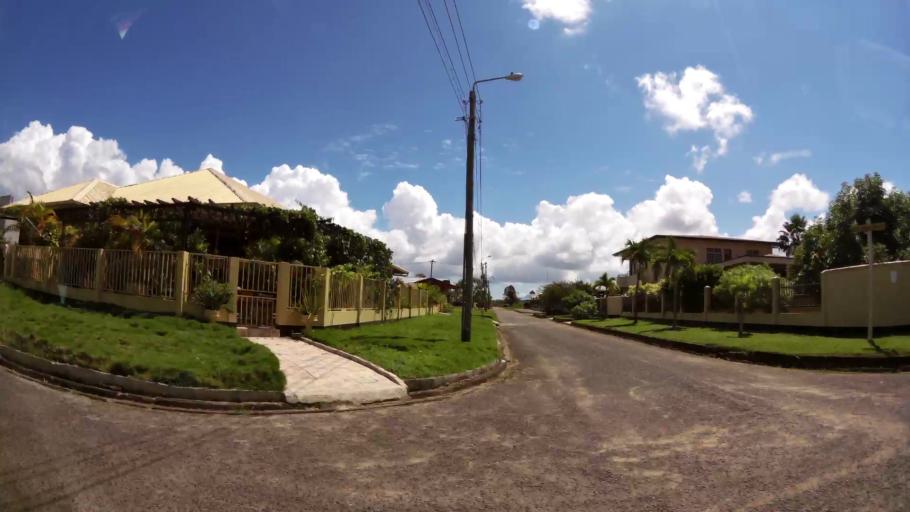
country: SR
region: Paramaribo
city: Paramaribo
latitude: 5.8603
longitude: -55.1305
